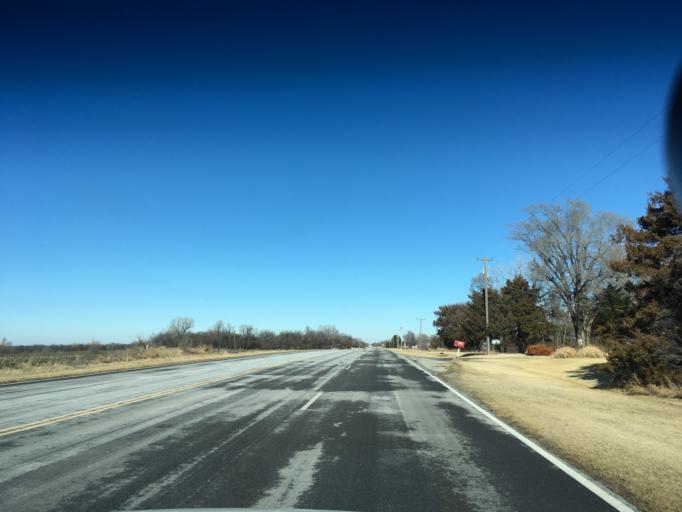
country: US
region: Kansas
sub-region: Harvey County
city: Sedgwick
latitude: 37.9238
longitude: -97.3364
